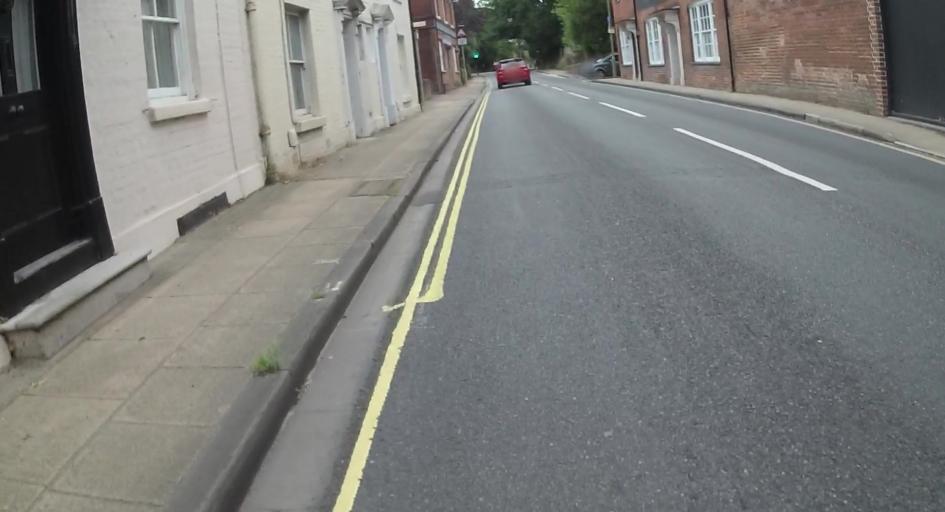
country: GB
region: England
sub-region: Hampshire
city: Winchester
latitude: 51.0499
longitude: -1.3228
